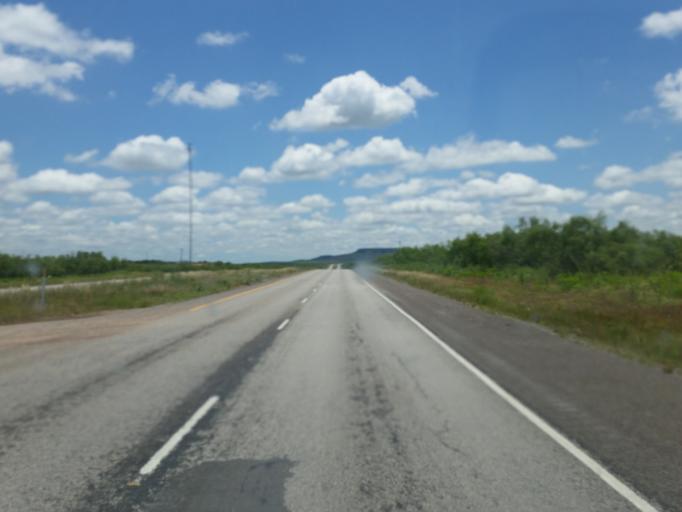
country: US
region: Texas
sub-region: Garza County
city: Post
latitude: 32.9866
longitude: -101.1326
